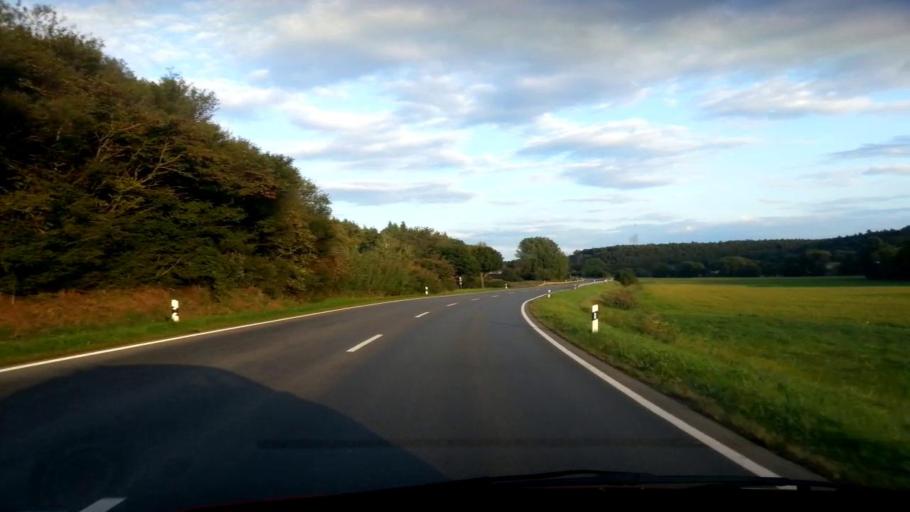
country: DE
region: Bavaria
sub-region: Upper Franconia
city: Burgwindheim
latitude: 49.8276
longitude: 10.6036
